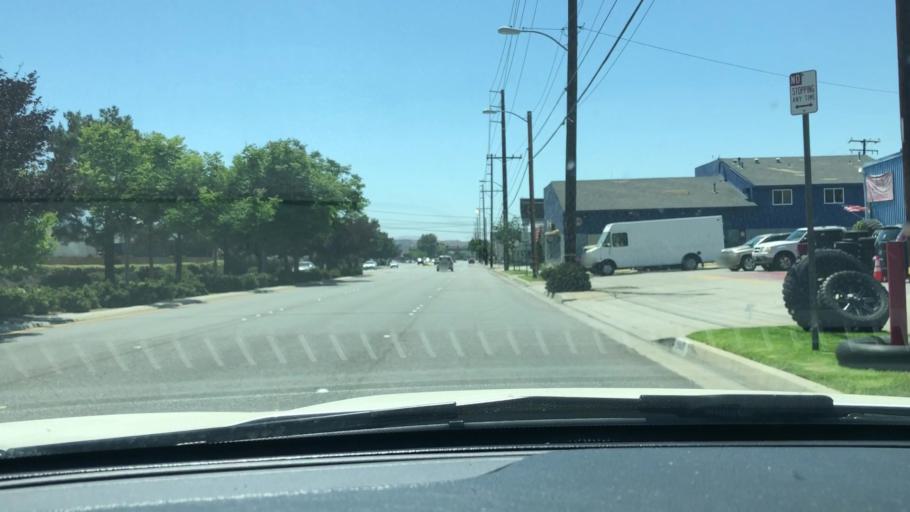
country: US
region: California
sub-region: Los Angeles County
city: Santa Clarita
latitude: 34.4213
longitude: -118.4947
